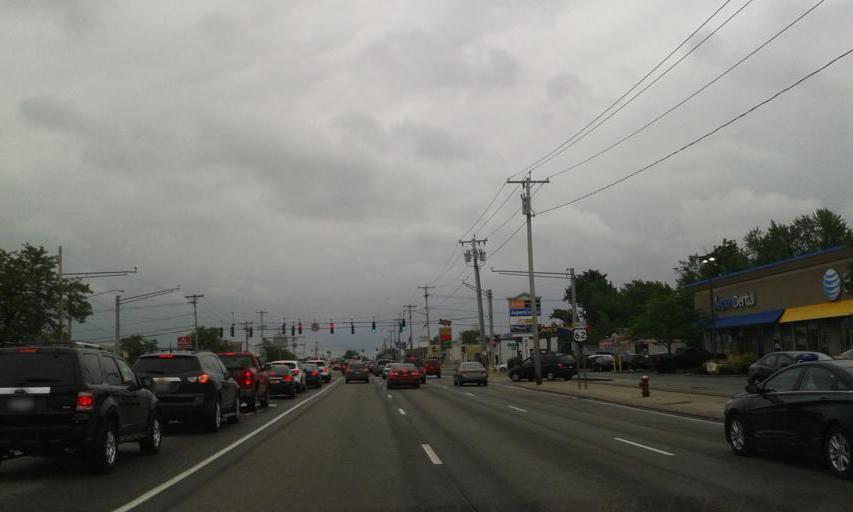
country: US
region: New York
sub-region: Erie County
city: Amherst
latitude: 43.0024
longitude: -78.8225
